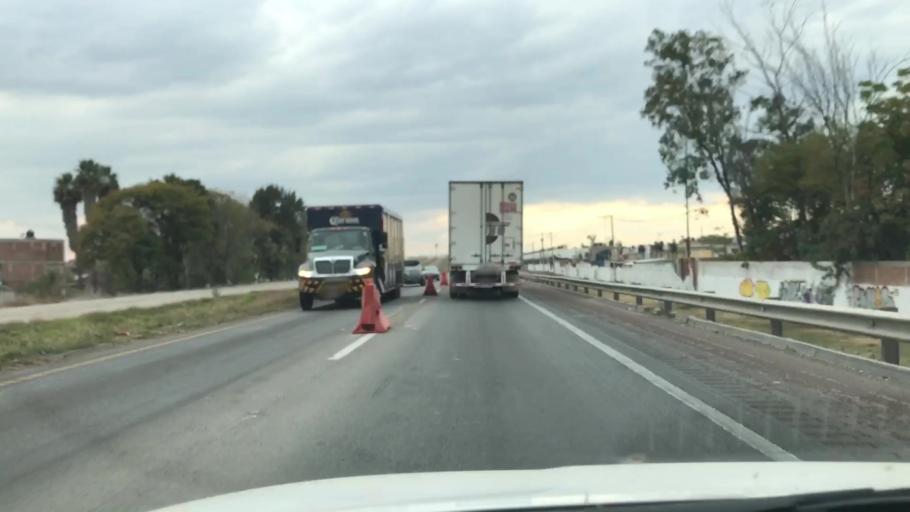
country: MX
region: Guanajuato
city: Irapuato
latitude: 20.6514
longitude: -101.3294
